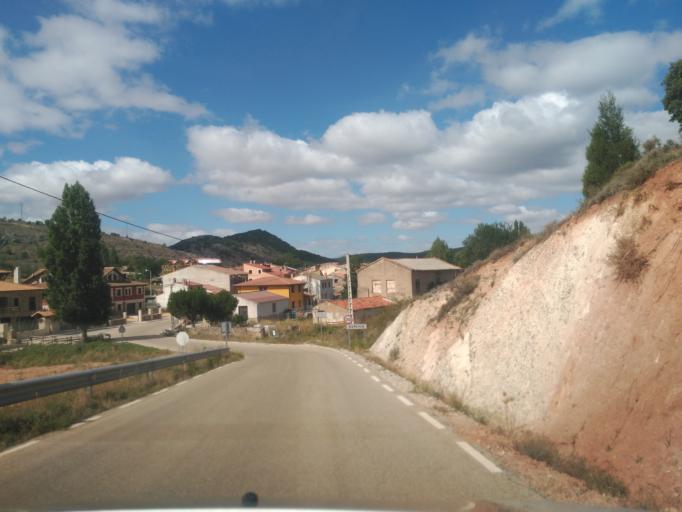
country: ES
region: Castille and Leon
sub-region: Provincia de Soria
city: Espejon
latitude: 41.8303
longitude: -3.2551
